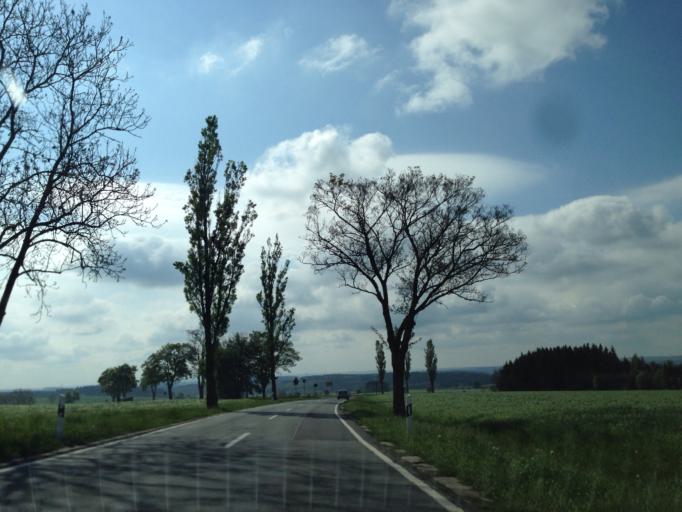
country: DE
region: Thuringia
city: Moxa
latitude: 50.6571
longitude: 11.6327
